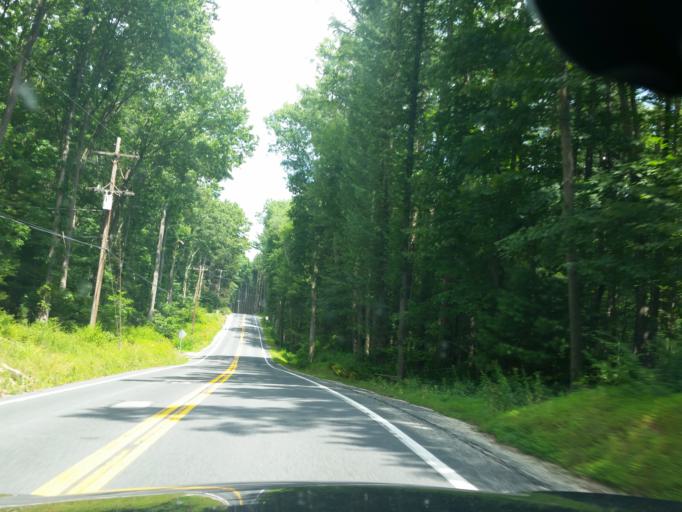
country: US
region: Pennsylvania
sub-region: Adams County
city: Biglerville
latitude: 40.0379
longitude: -77.2799
